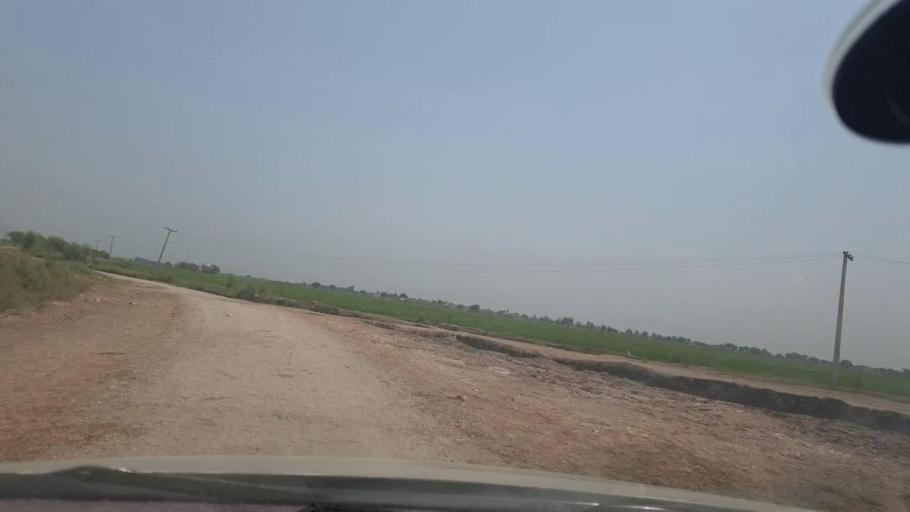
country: PK
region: Sindh
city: Jacobabad
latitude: 28.1681
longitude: 68.3926
